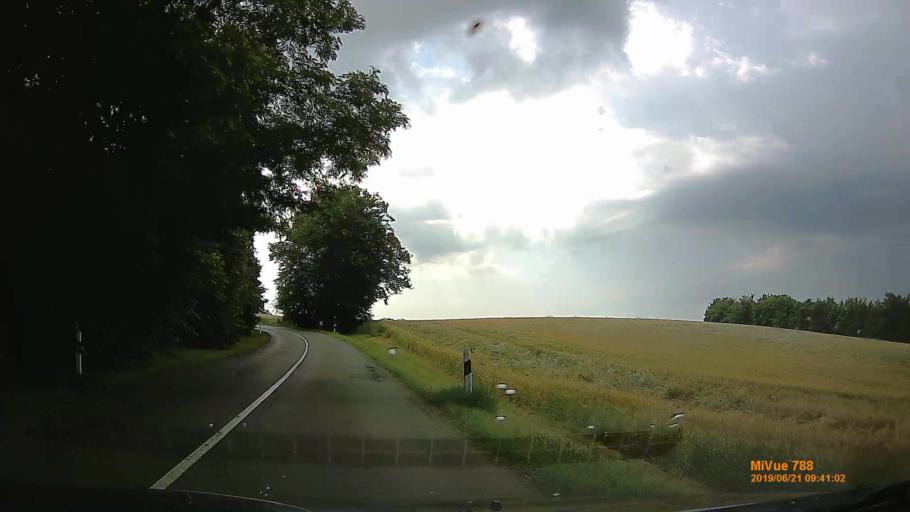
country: HU
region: Somogy
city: Taszar
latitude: 46.2922
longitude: 17.9514
